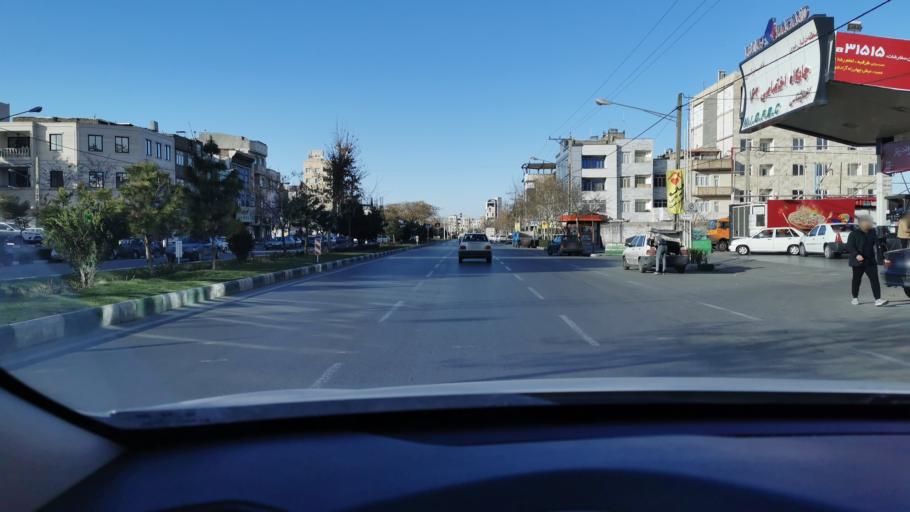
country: IR
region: Razavi Khorasan
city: Mashhad
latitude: 36.3367
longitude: 59.5218
